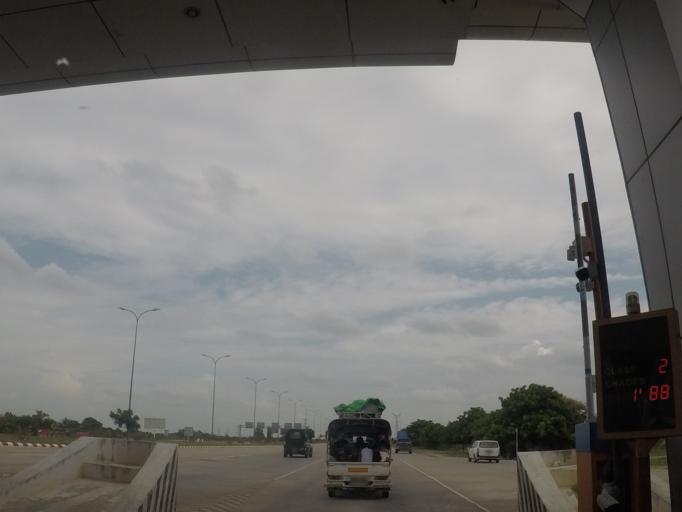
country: MM
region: Sagain
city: Sagaing
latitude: 21.7541
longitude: 95.9764
